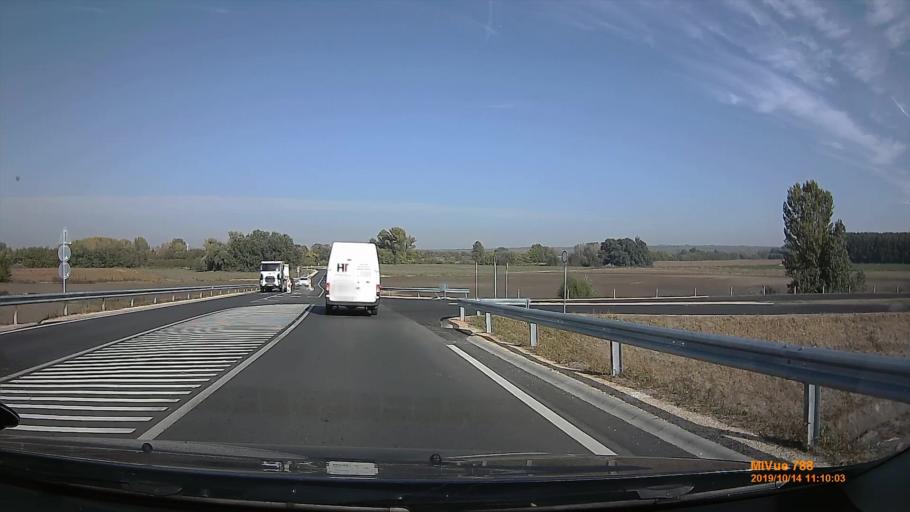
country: HU
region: Pest
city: Peteri
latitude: 47.3727
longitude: 19.4231
